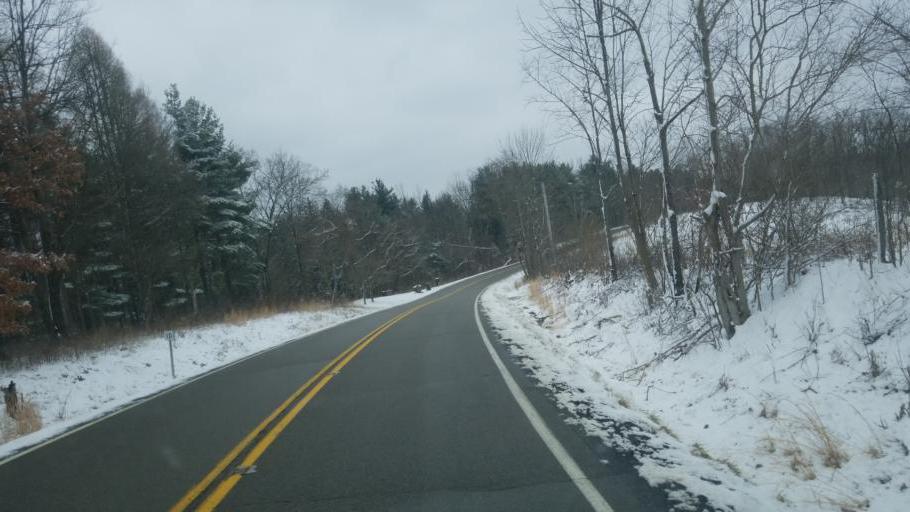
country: US
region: Ohio
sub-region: Knox County
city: Oak Hill
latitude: 40.3988
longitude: -82.1252
